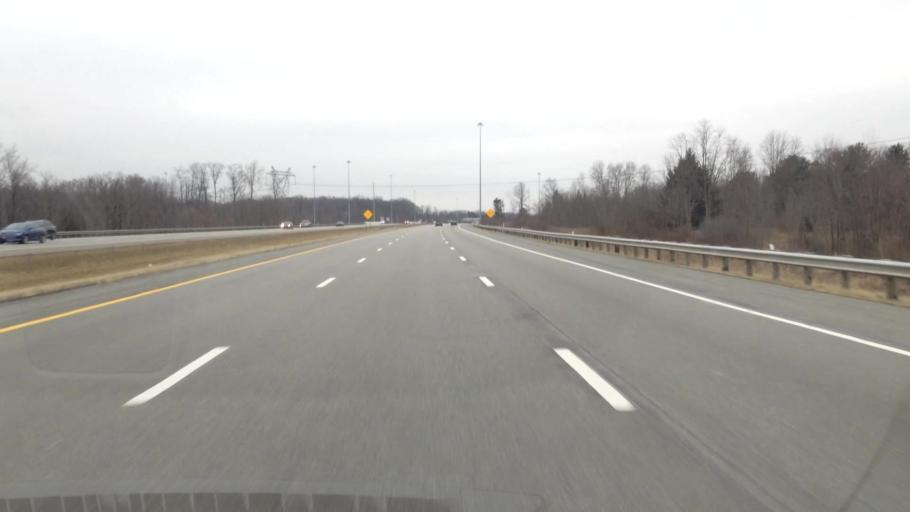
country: US
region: Ohio
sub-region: Medina County
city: Medina
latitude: 41.1657
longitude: -81.7856
